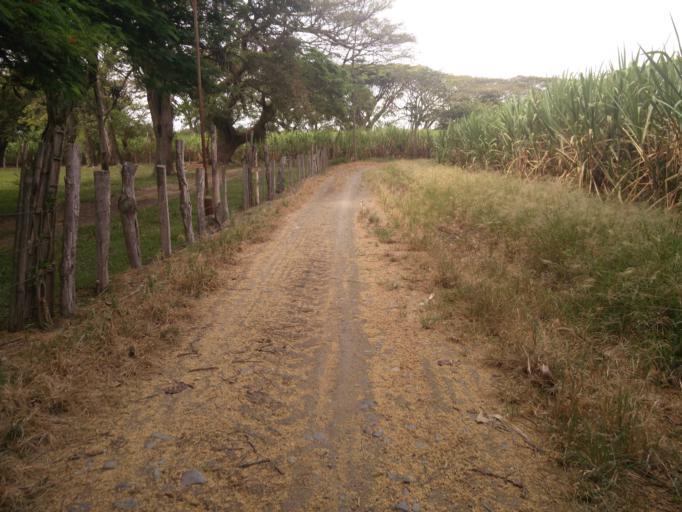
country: CO
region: Valle del Cauca
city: Buga
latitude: 3.8894
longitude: -76.3240
